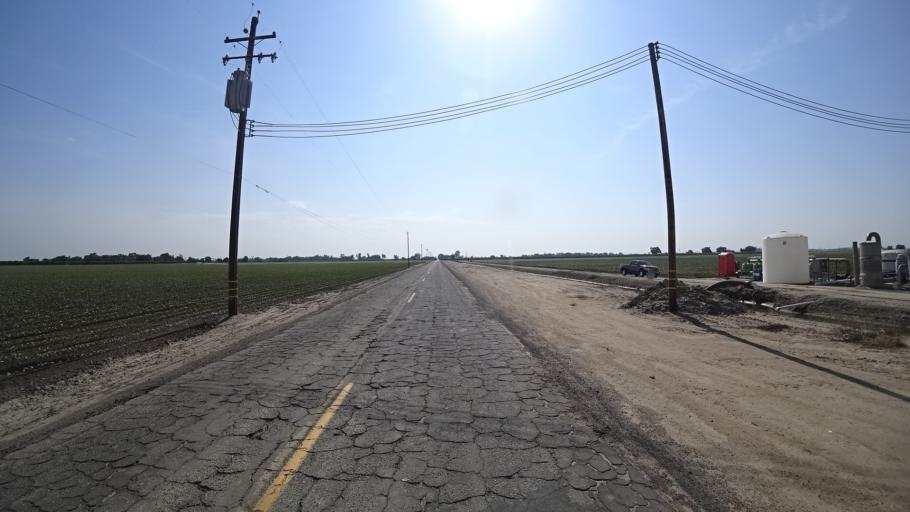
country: US
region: California
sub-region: Kings County
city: Lemoore
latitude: 36.3206
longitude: -119.8330
